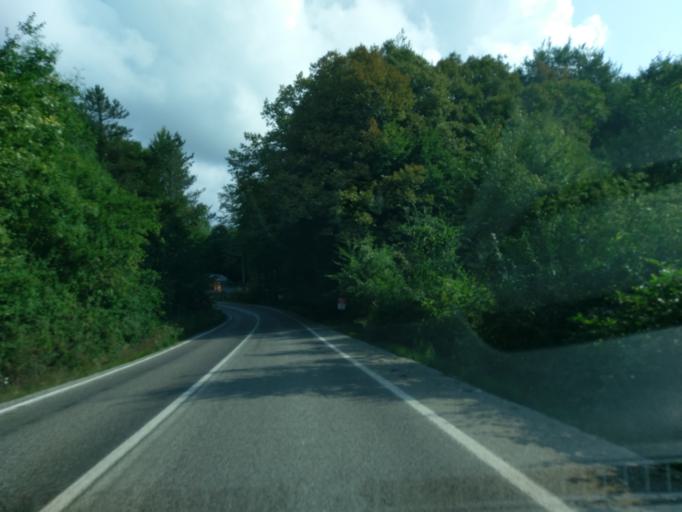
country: TR
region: Sinop
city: Ayancik
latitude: 41.8799
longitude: 34.5129
